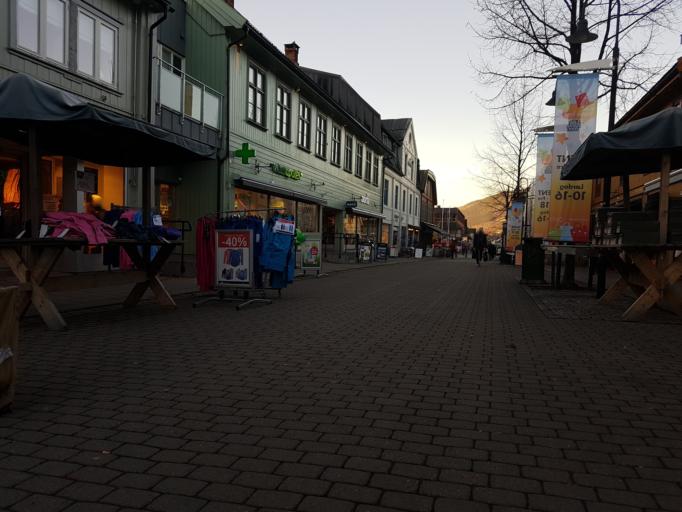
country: NO
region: Oppland
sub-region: Lillehammer
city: Lillehammer
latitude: 61.1167
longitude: 10.4652
